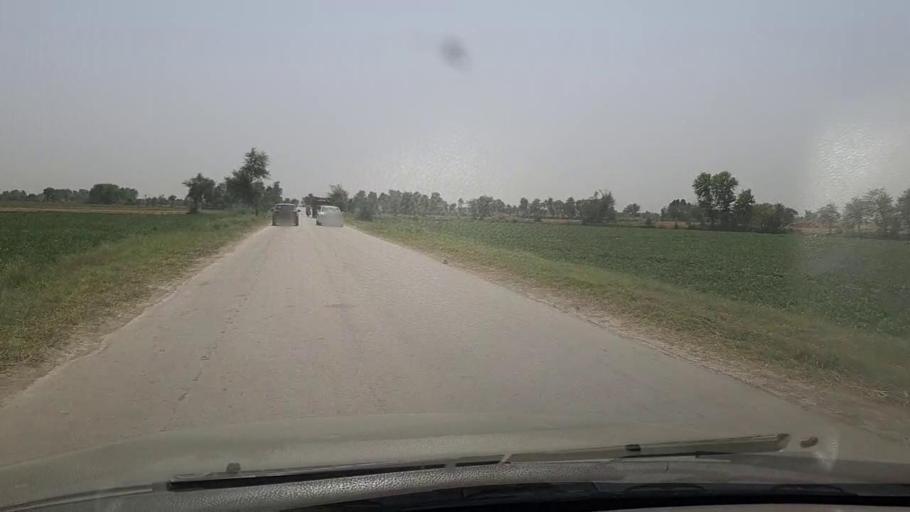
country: PK
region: Sindh
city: Kambar
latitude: 27.6233
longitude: 68.0236
